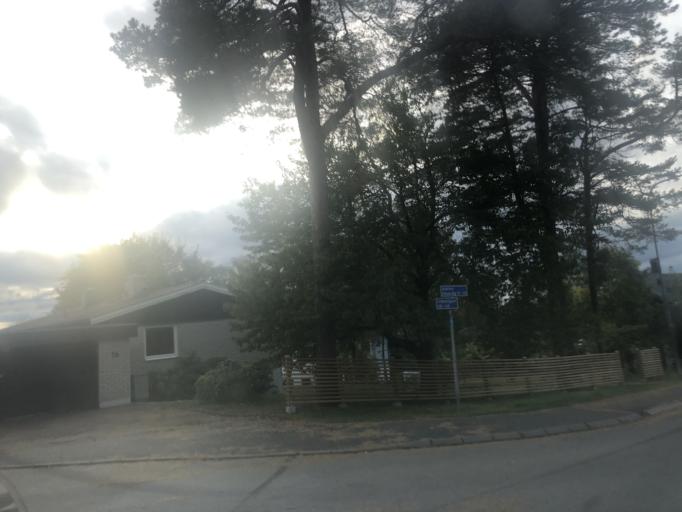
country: SE
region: Vaestra Goetaland
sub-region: Goteborg
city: Billdal
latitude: 57.6290
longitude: 11.9487
